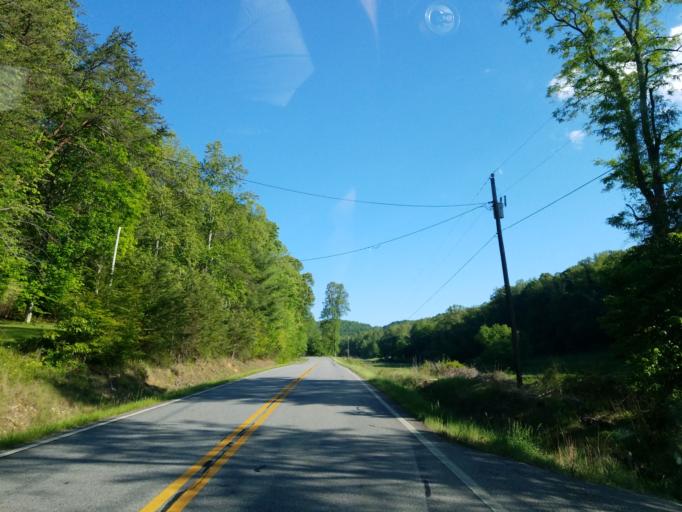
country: US
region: Georgia
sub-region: Fannin County
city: Blue Ridge
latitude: 34.8278
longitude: -84.1902
